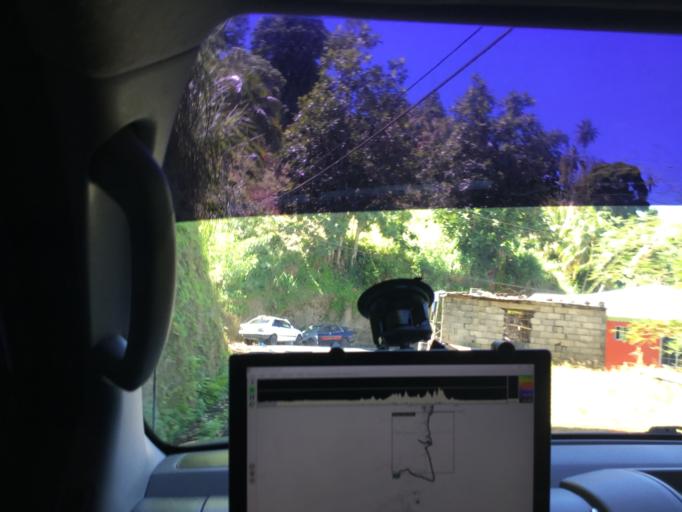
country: VC
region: Charlotte
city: Byera Village
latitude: 13.2442
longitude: -61.1385
